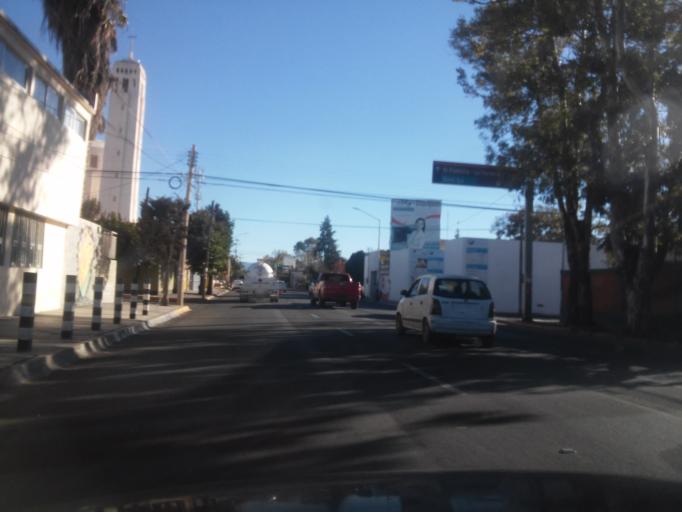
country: MX
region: Durango
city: Victoria de Durango
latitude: 24.0342
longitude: -104.6573
